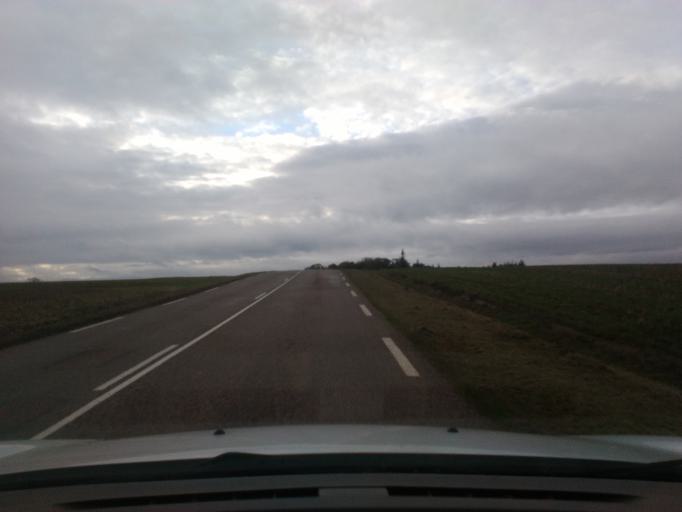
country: FR
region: Lorraine
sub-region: Departement des Vosges
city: Rambervillers
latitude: 48.3559
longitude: 6.5942
